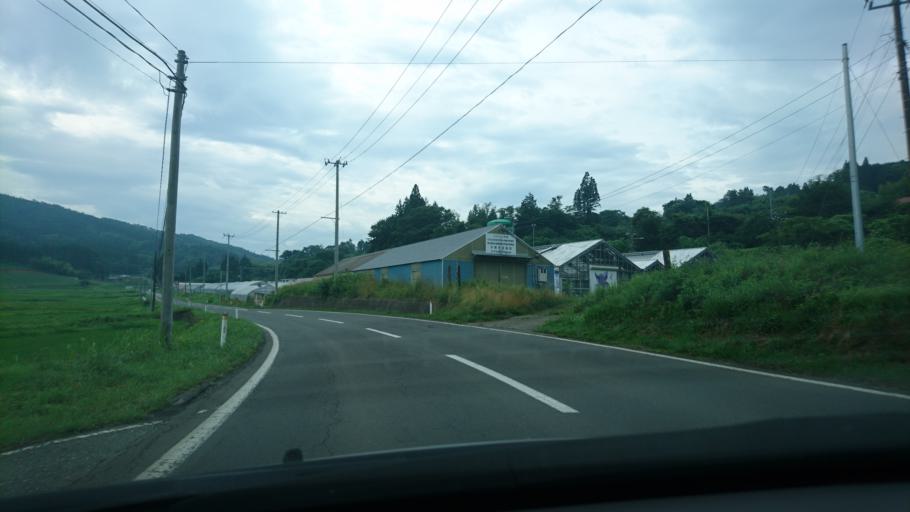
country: JP
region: Iwate
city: Ichinoseki
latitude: 38.9282
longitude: 141.4196
